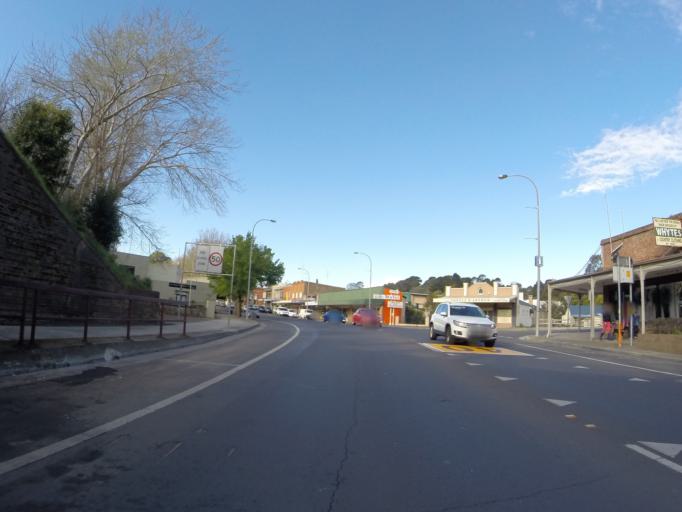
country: AU
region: New South Wales
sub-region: Wingecarribee
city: Moss Vale
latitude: -34.5507
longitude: 150.3701
